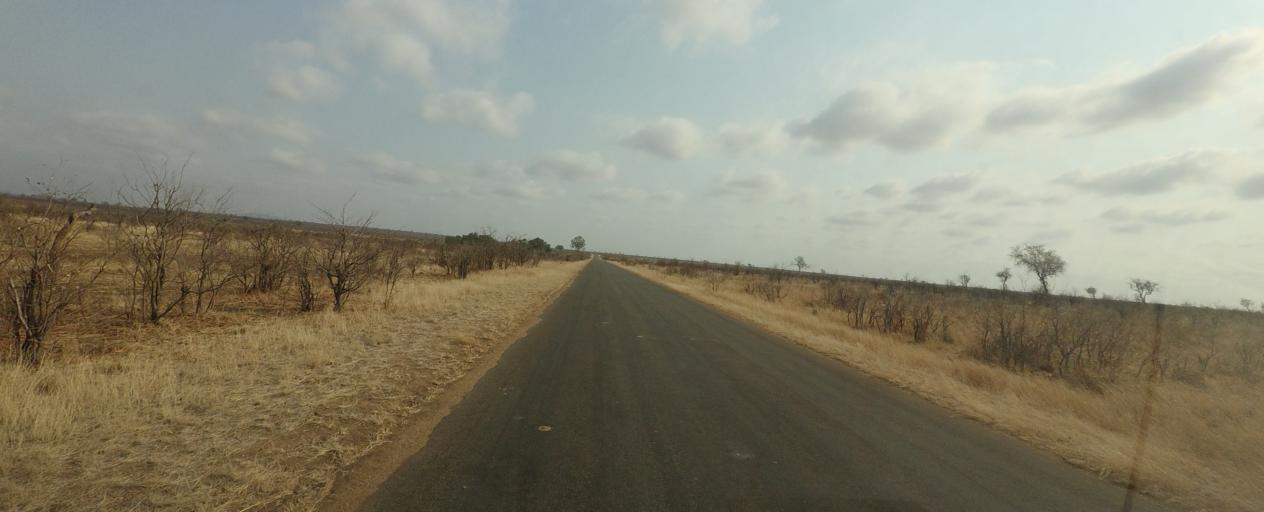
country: ZA
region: Limpopo
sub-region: Vhembe District Municipality
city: Mutale
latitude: -22.9109
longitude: 31.2531
